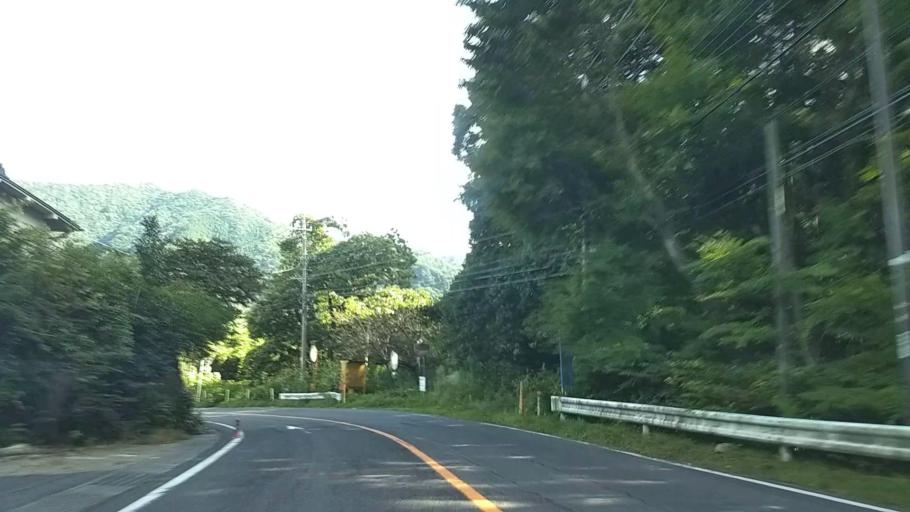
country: JP
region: Tochigi
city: Imaichi
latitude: 36.8571
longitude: 139.7274
